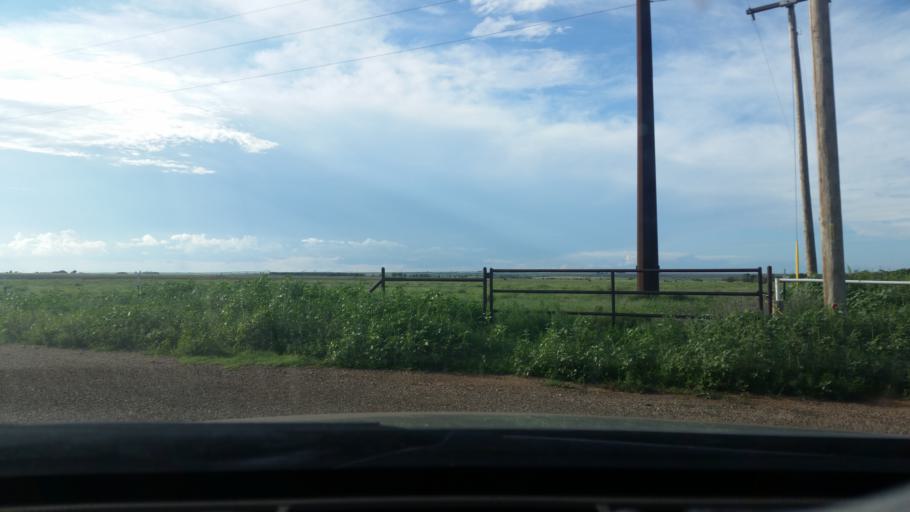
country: US
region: New Mexico
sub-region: Curry County
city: Clovis
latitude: 34.5065
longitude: -103.1788
